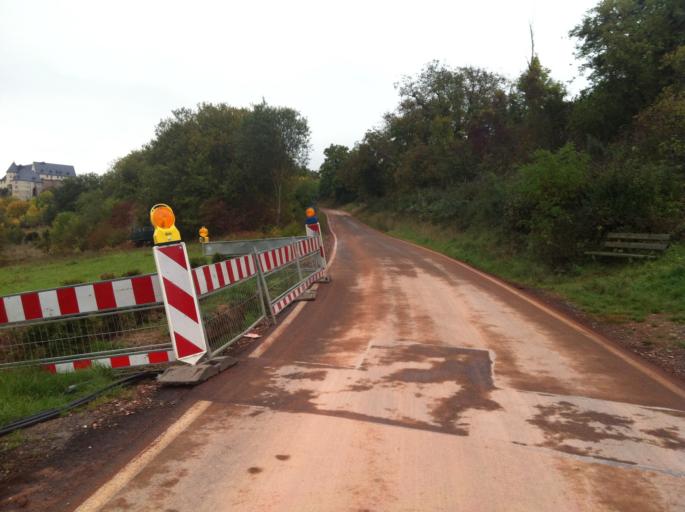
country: DE
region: Rheinland-Pfalz
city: Bad Munster am Stein-Ebernburg
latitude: 49.8062
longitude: 7.8323
